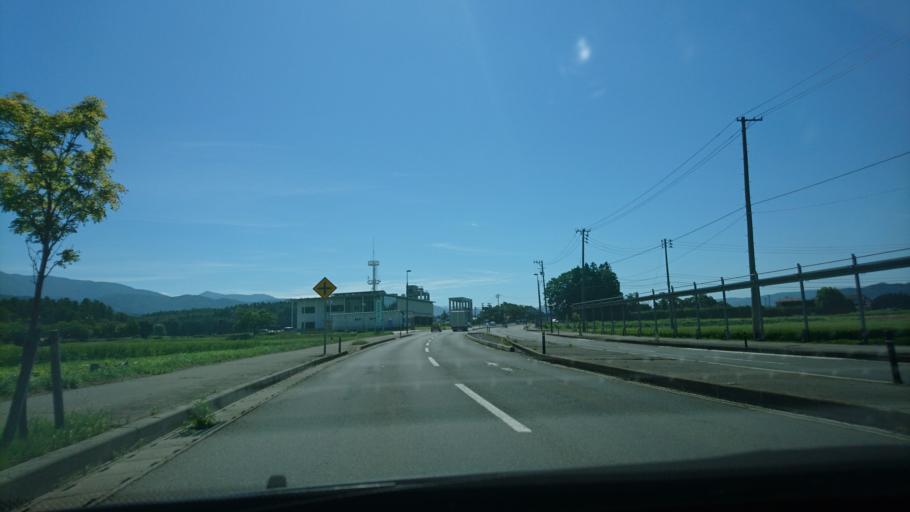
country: JP
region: Iwate
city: Tono
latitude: 39.3306
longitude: 141.5614
